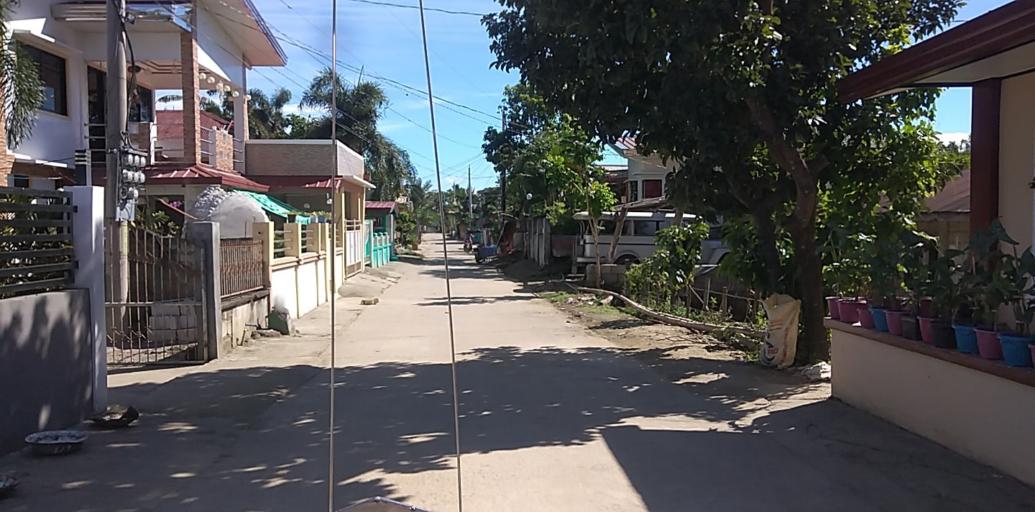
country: PH
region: Central Luzon
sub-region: Province of Pampanga
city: San Nicolas
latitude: 15.0640
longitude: 120.8117
